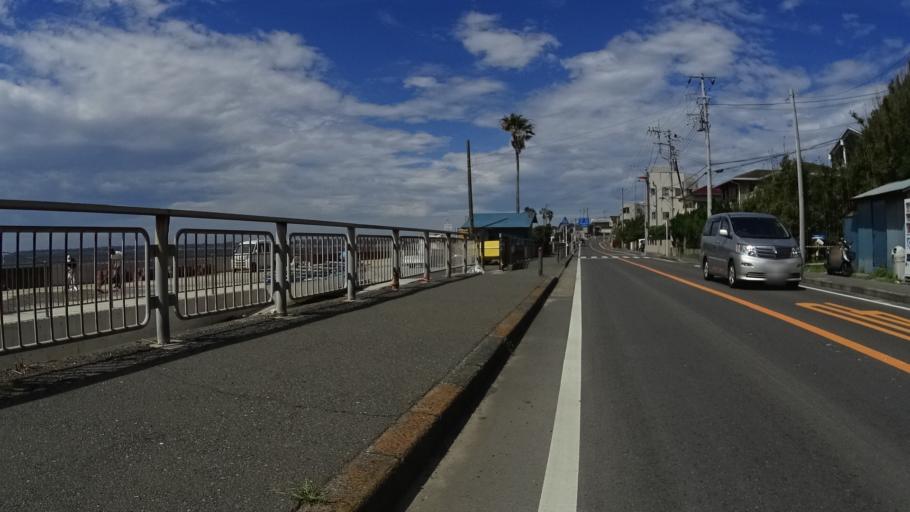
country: JP
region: Kanagawa
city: Yokosuka
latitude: 35.2088
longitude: 139.6891
